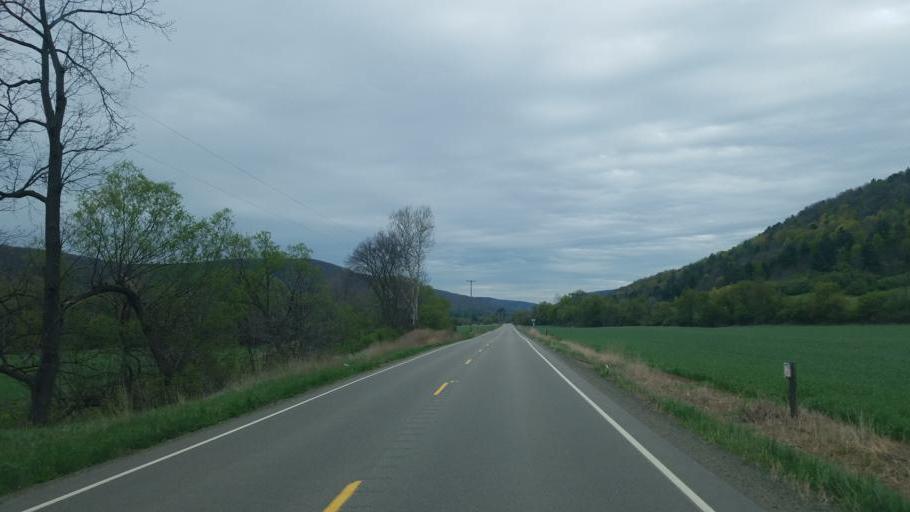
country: US
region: Pennsylvania
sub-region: Tioga County
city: Westfield
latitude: 41.9834
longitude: -77.4773
